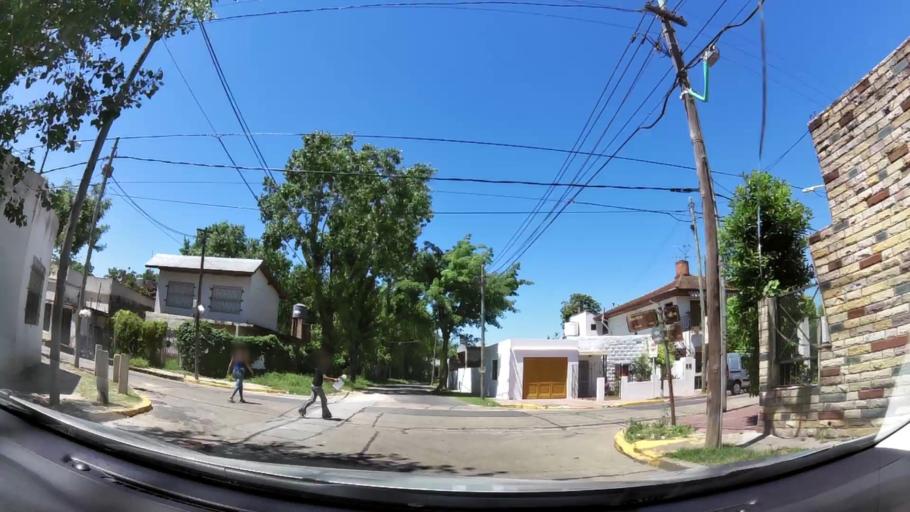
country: AR
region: Buenos Aires
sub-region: Partido de Tigre
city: Tigre
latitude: -34.4540
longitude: -58.5517
